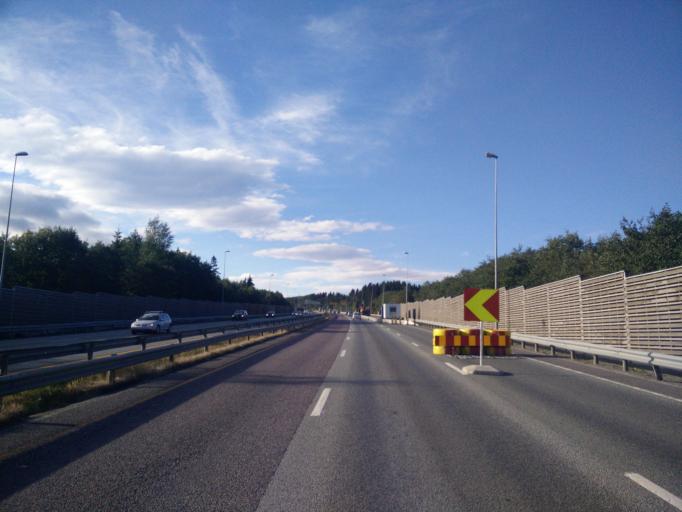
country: NO
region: Sor-Trondelag
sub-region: Trondheim
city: Trondheim
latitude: 63.3868
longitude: 10.3787
